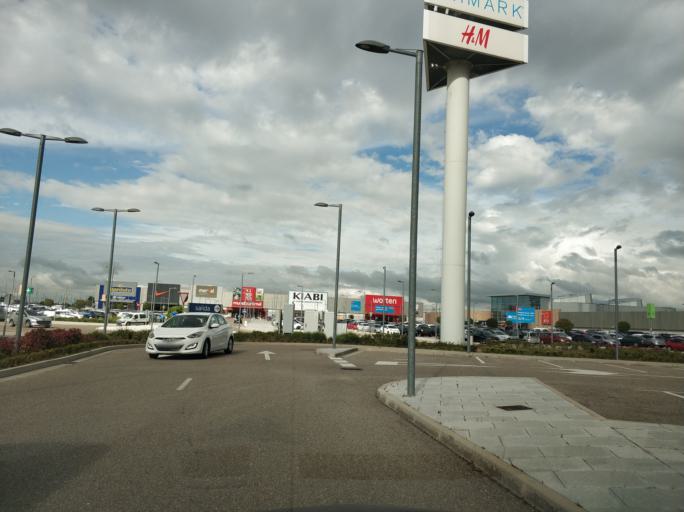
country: ES
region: Castille and Leon
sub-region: Provincia de Valladolid
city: Arroyo
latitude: 41.6295
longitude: -4.7873
